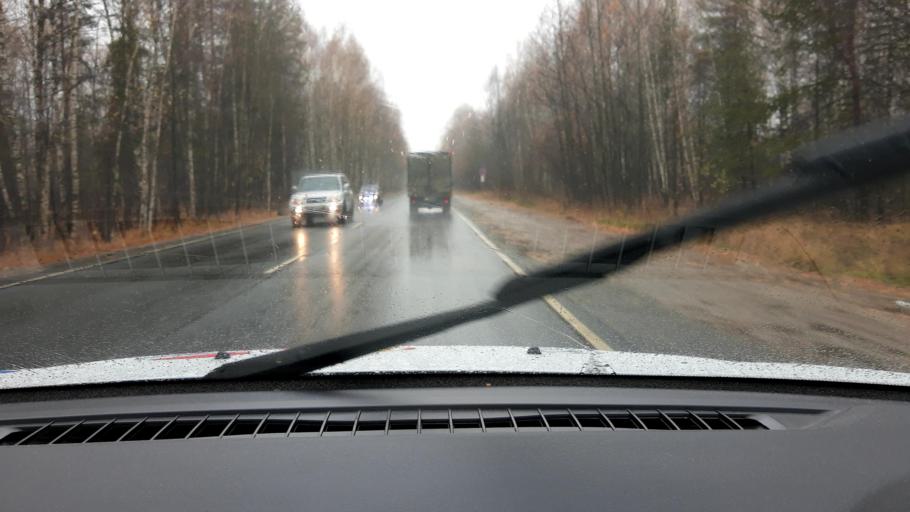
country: RU
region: Nizjnij Novgorod
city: Gorbatovka
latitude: 56.2620
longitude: 43.6972
